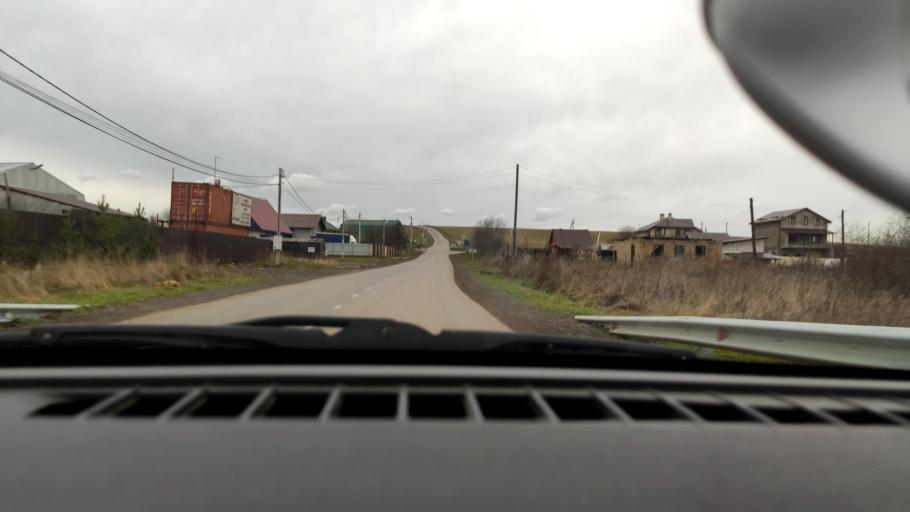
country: RU
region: Perm
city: Ferma
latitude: 57.9188
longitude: 56.3294
